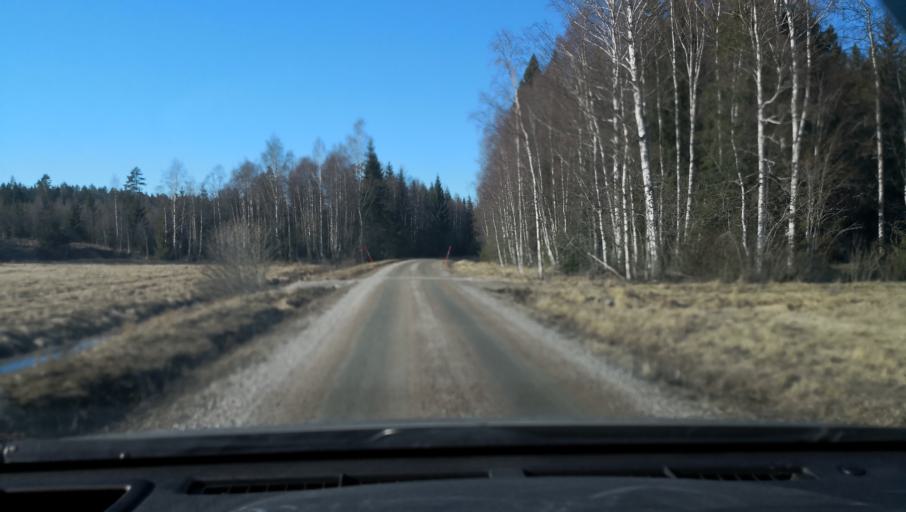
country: SE
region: Vaestmanland
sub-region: Sala Kommun
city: Sala
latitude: 60.1341
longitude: 16.6503
